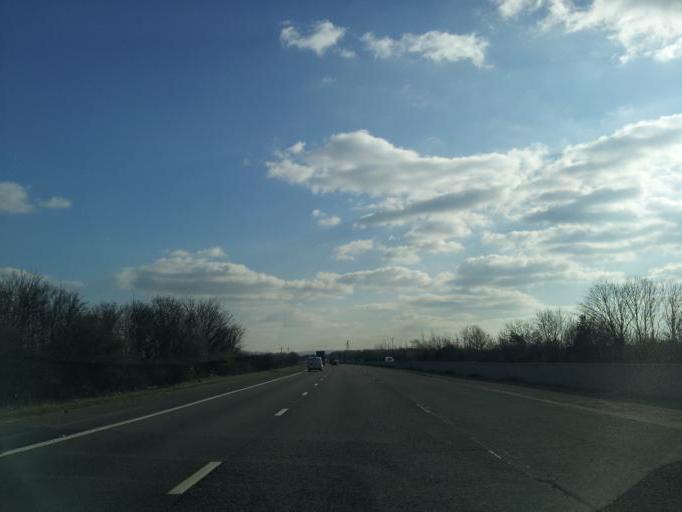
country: GB
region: England
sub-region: Somerset
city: North Petherton
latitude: 51.0905
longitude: -3.0037
